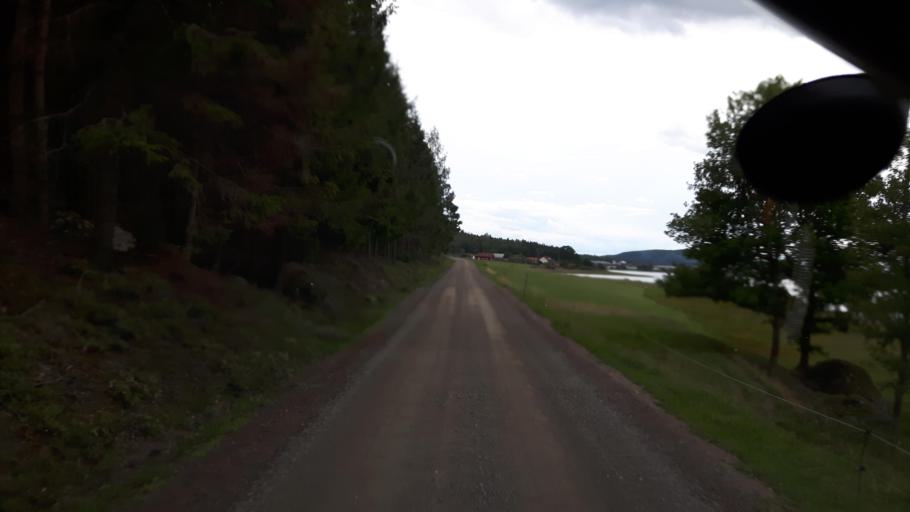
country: SE
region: OEstergoetland
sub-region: Kinda Kommun
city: Kisa
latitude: 58.0168
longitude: 15.6536
